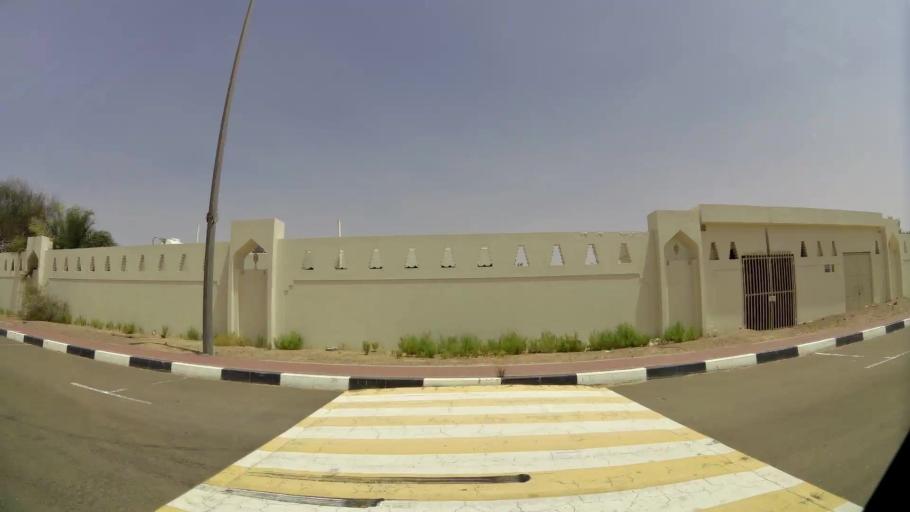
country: AE
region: Abu Dhabi
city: Al Ain
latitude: 24.1927
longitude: 55.6806
